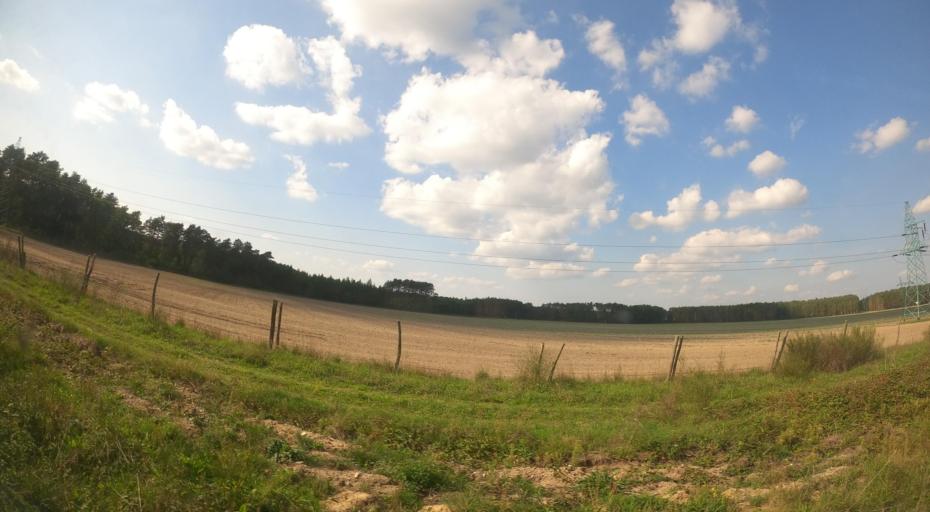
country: PL
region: Lubusz
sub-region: Powiat zielonogorski
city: Swidnica
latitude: 51.9052
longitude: 15.3191
